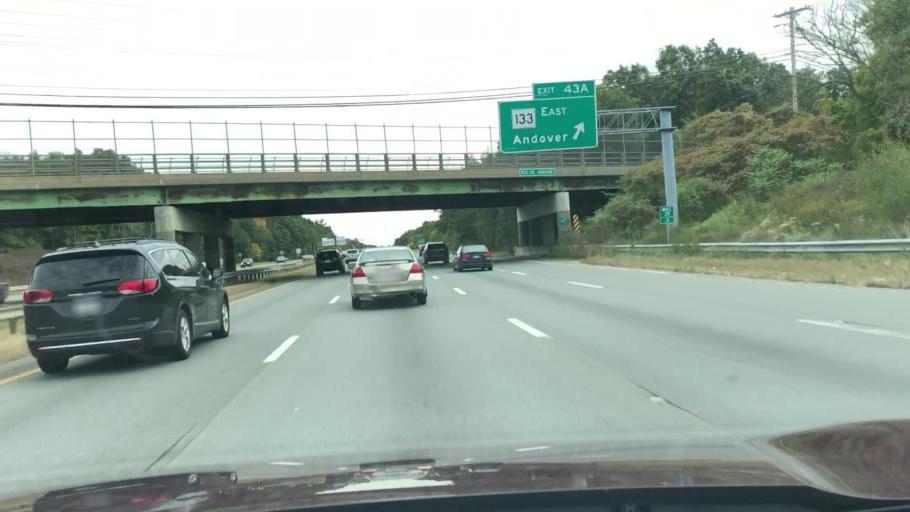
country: US
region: Massachusetts
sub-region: Essex County
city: Andover
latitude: 42.6465
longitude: -71.1864
